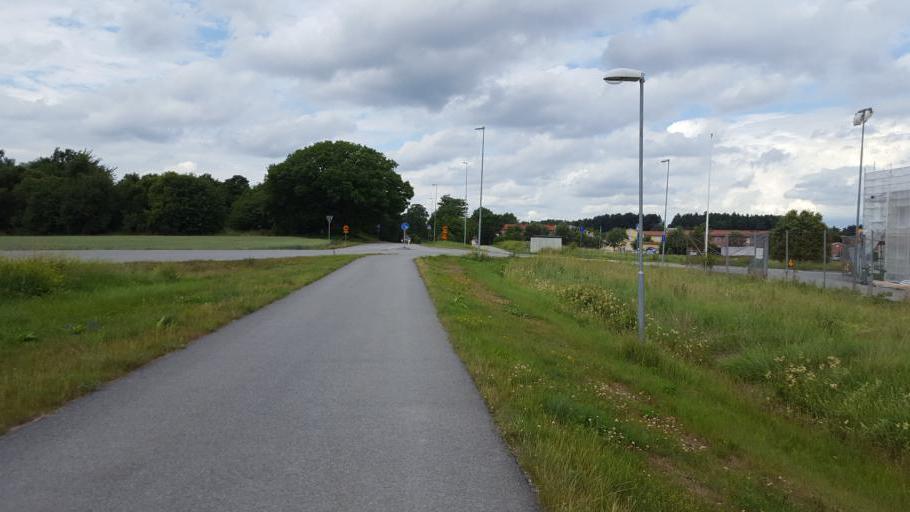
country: SE
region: Stockholm
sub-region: Upplands Vasby Kommun
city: Upplands Vaesby
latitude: 59.5041
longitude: 17.8881
